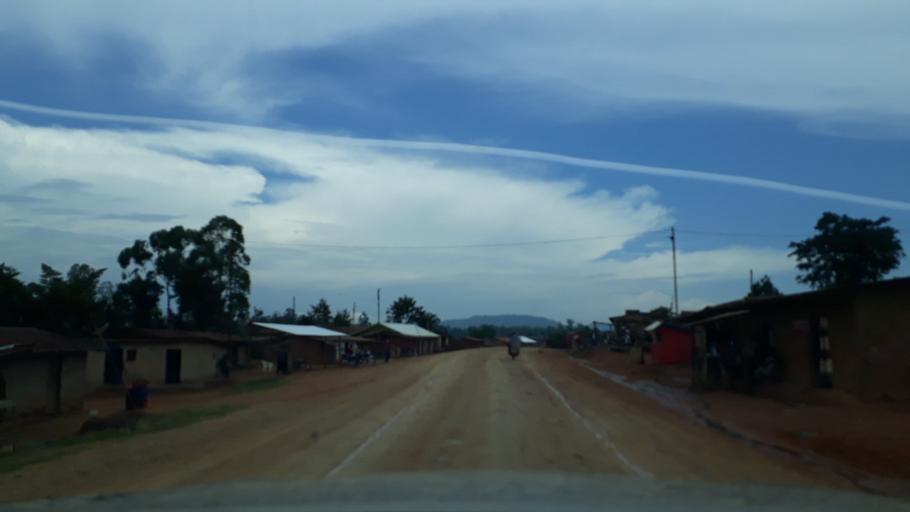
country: CD
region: Eastern Province
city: Bunia
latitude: 1.6436
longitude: 30.2687
